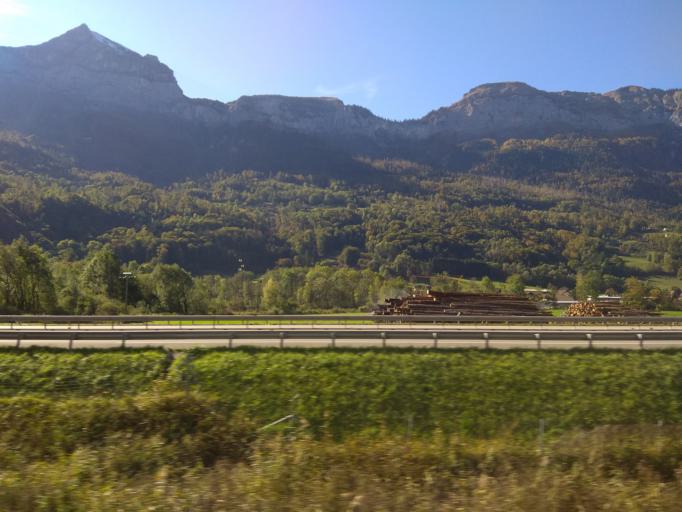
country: FR
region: Rhone-Alpes
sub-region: Departement de la Haute-Savoie
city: Magland
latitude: 46.0027
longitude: 6.6289
